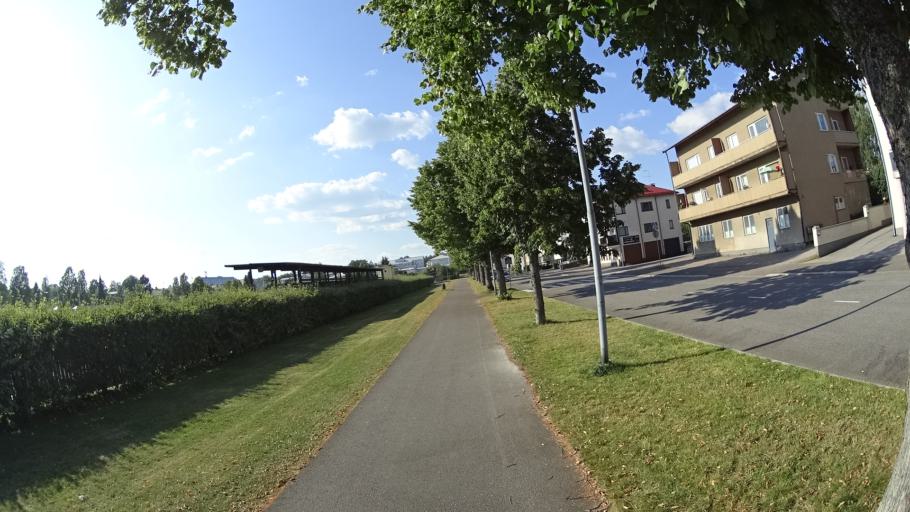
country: FI
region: Uusimaa
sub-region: Porvoo
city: Porvoo
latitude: 60.3937
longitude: 25.6743
